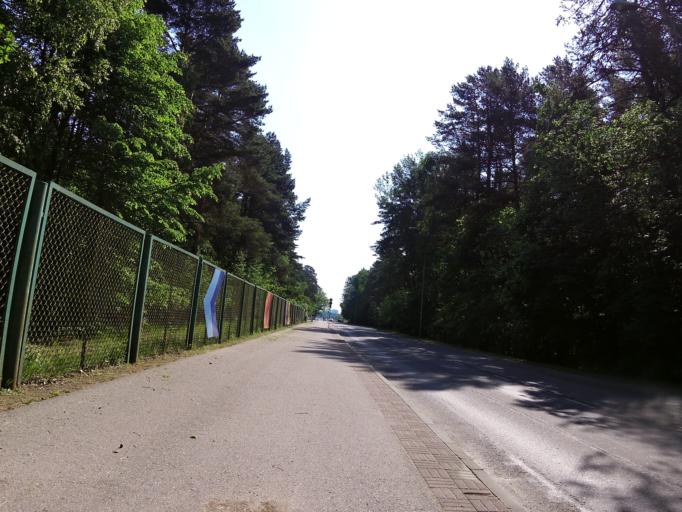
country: EE
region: Harju
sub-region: Saue vald
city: Laagri
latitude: 59.4307
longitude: 24.6454
